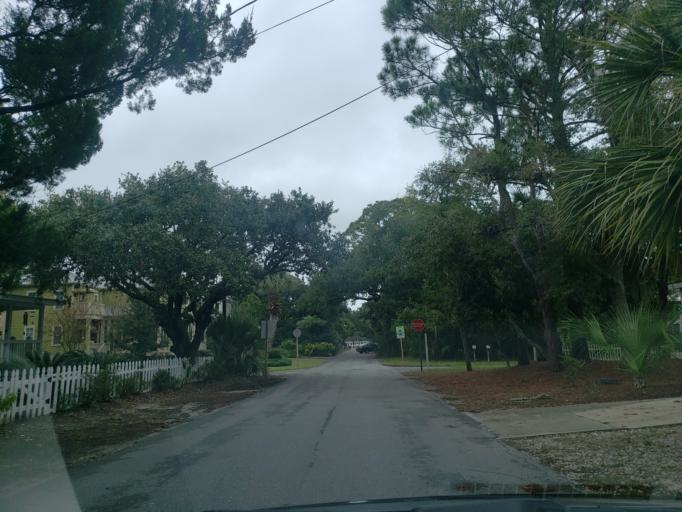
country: US
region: Georgia
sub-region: Chatham County
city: Tybee Island
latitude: 32.0052
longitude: -80.8456
